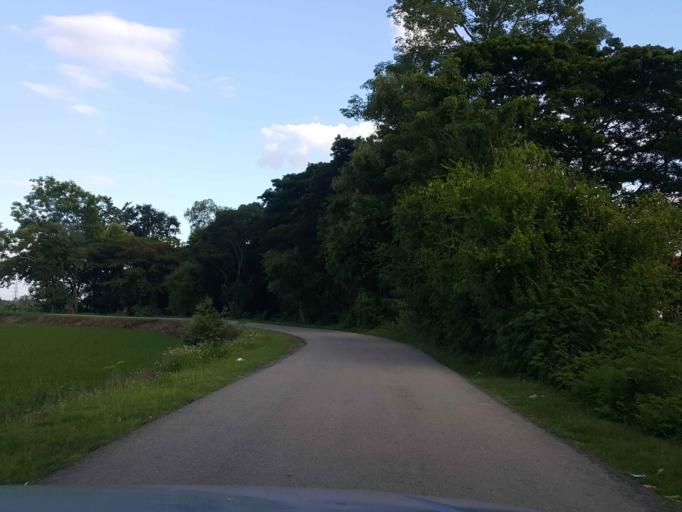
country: TH
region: Chiang Mai
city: San Sai
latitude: 18.9111
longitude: 98.9783
